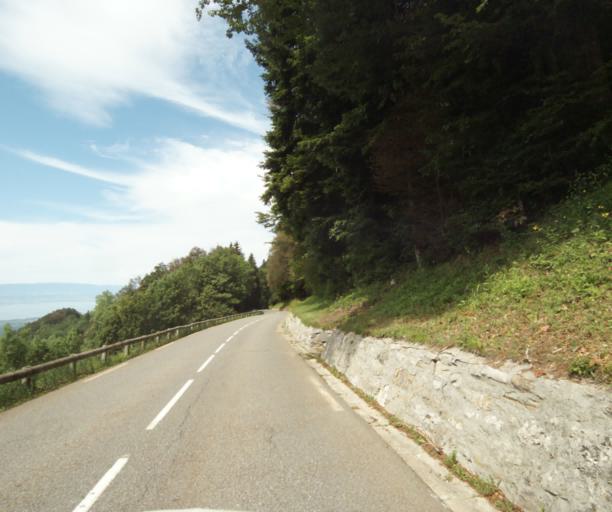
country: FR
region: Rhone-Alpes
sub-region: Departement de la Haute-Savoie
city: Perrignier
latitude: 46.2668
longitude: 6.4520
